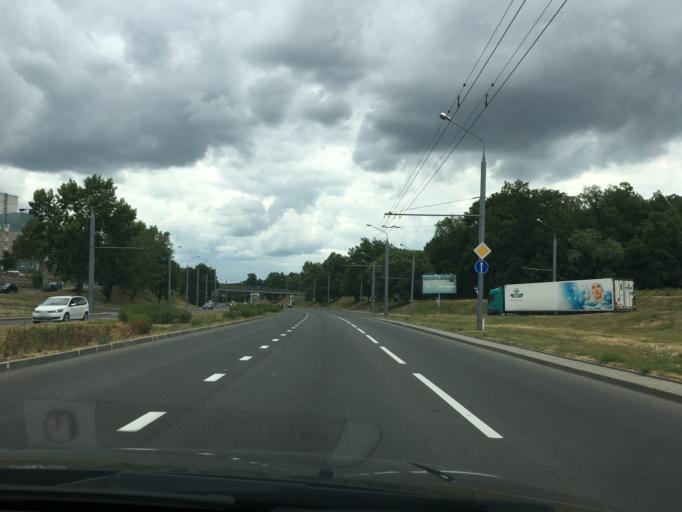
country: BY
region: Grodnenskaya
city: Hrodna
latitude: 53.6537
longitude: 23.8556
